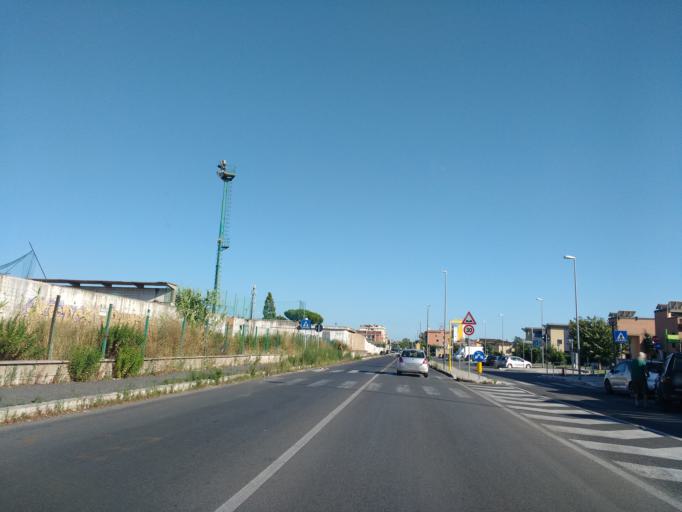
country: IT
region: Latium
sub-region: Citta metropolitana di Roma Capitale
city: Acilia-Castel Fusano-Ostia Antica
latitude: 41.7732
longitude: 12.3540
